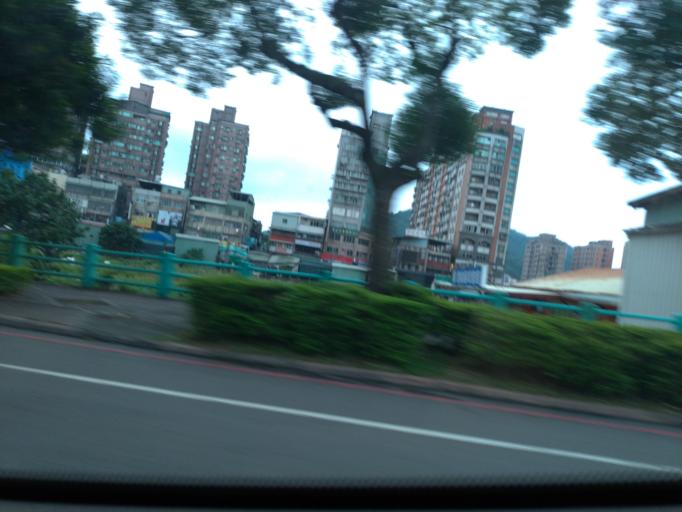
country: TW
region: Taiwan
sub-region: Taoyuan
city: Taoyuan
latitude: 24.9341
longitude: 121.3751
